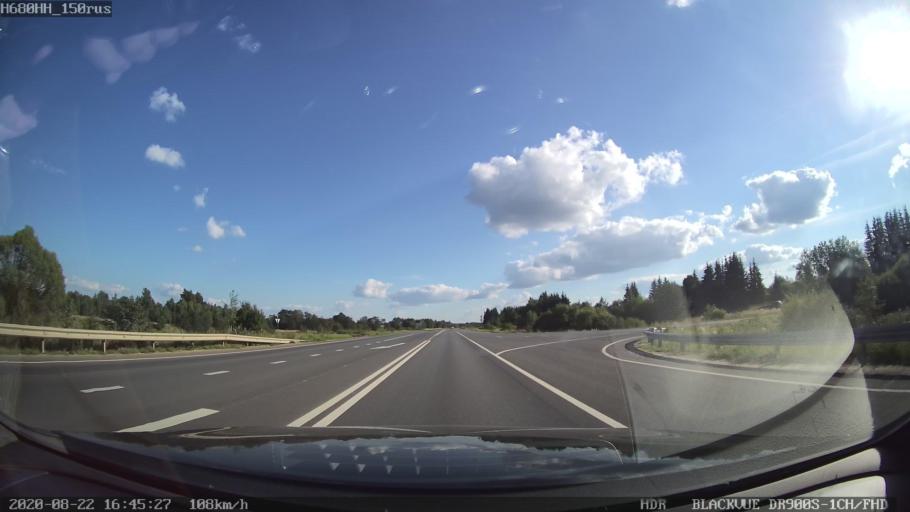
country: RU
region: Tverskaya
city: Rameshki
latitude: 57.2971
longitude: 36.0909
